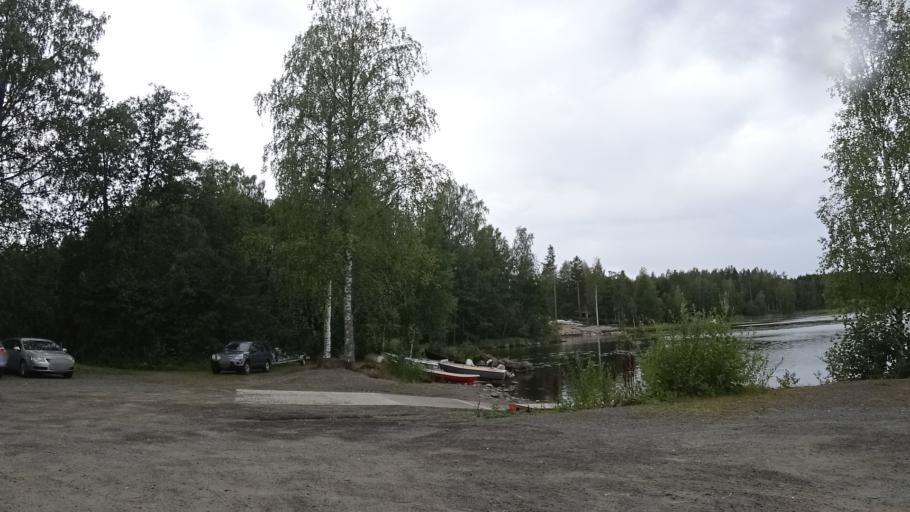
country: FI
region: North Karelia
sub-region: Keski-Karjala
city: Kesaelahti
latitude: 62.0964
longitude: 29.8747
